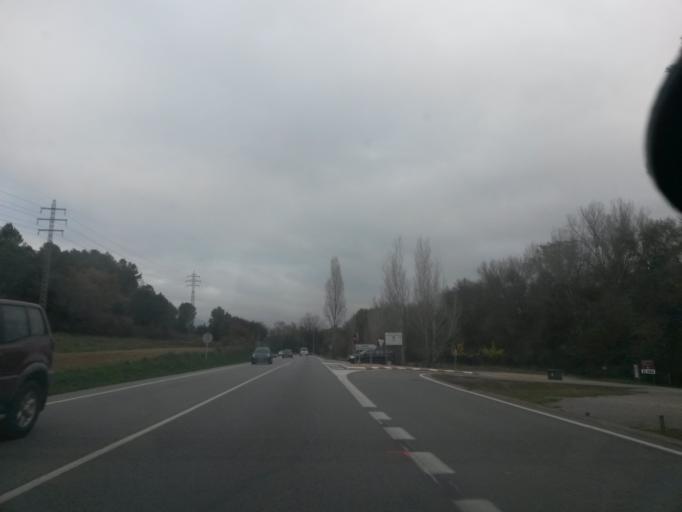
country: ES
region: Catalonia
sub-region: Provincia de Girona
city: Porqueres
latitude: 42.1607
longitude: 2.7456
